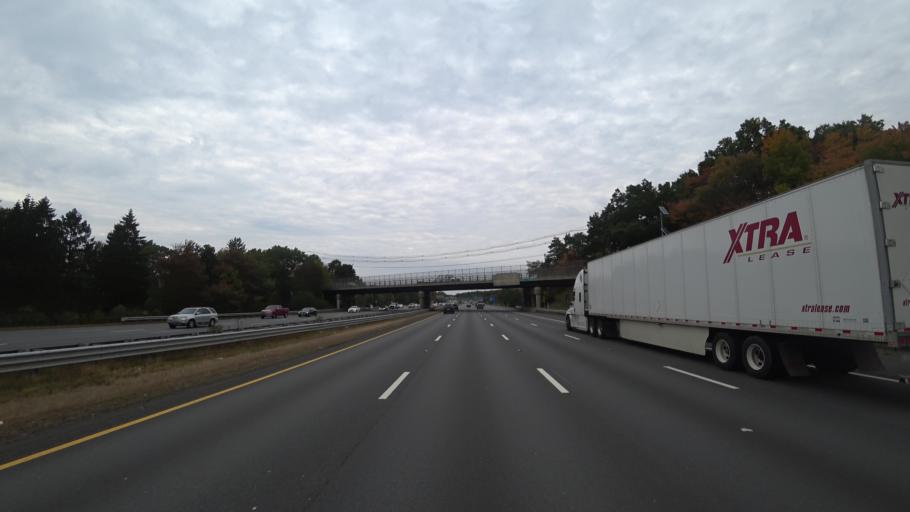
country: US
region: Massachusetts
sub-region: Middlesex County
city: Wilmington
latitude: 42.5326
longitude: -71.1356
